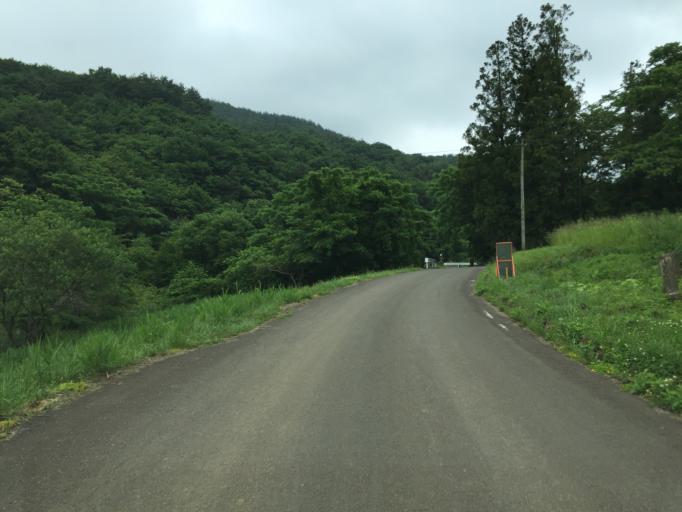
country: JP
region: Fukushima
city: Yanagawamachi-saiwaicho
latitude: 37.7840
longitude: 140.6994
